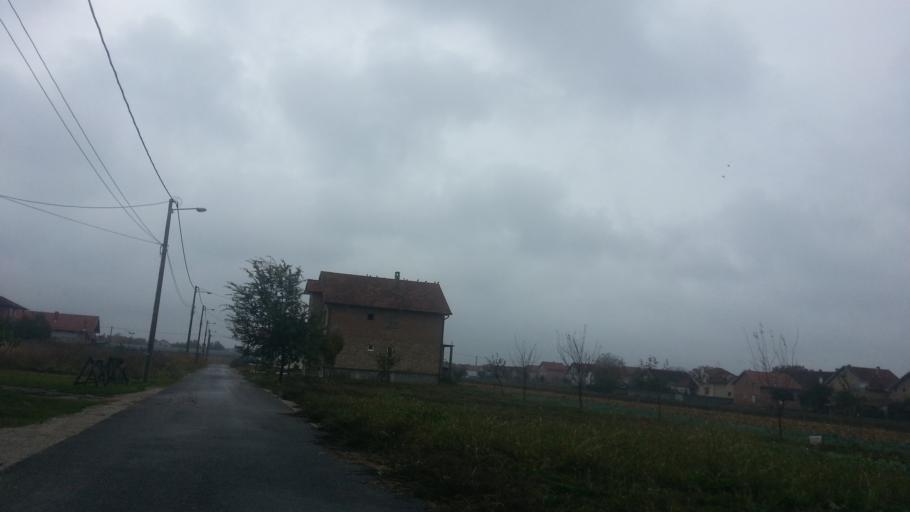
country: RS
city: Novi Banovci
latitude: 44.9042
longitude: 20.2980
